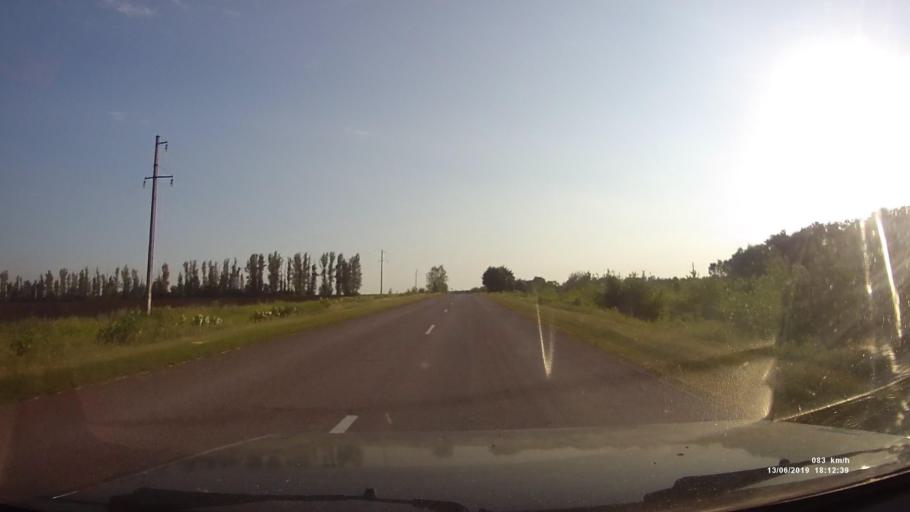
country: RU
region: Rostov
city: Kazanskaya
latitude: 49.9440
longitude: 41.4072
